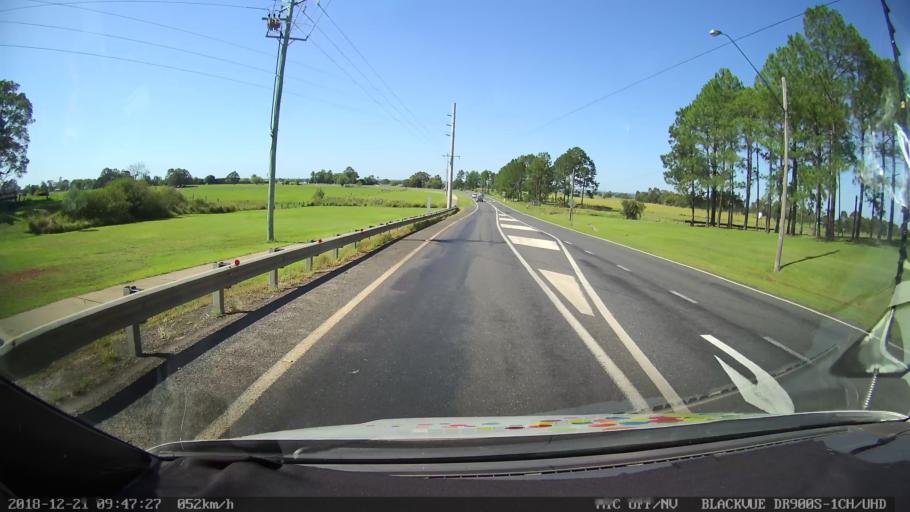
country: AU
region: New South Wales
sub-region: Clarence Valley
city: Grafton
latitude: -29.6459
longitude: 152.9273
